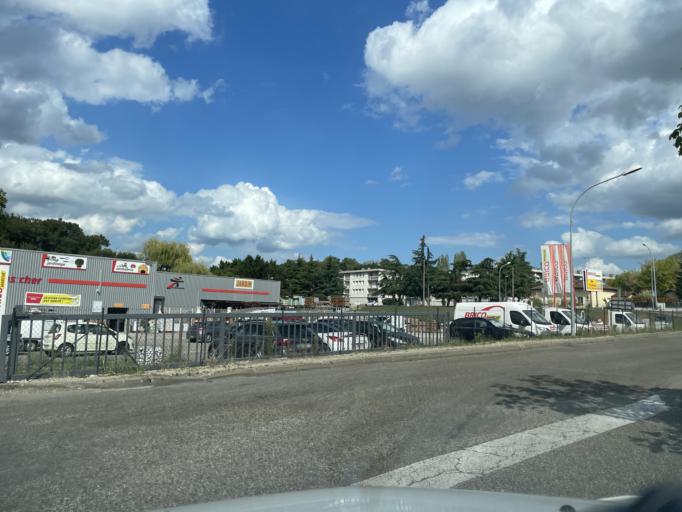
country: FR
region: Aquitaine
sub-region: Departement du Lot-et-Garonne
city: Casteljaloux
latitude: 44.3196
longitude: 0.0932
